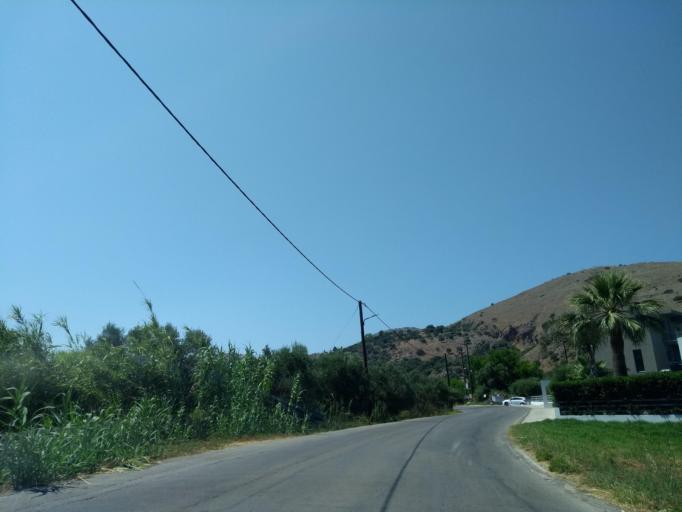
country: GR
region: Crete
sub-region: Nomos Chanias
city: Georgioupolis
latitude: 35.3654
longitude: 24.2570
